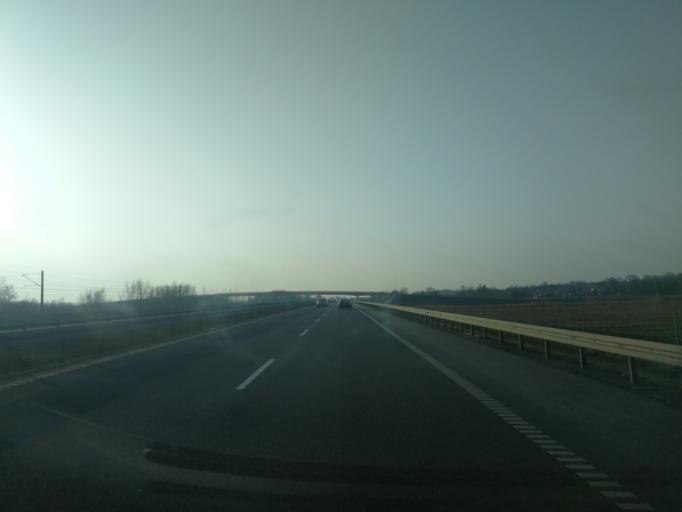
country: PL
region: Warmian-Masurian Voivodeship
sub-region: Powiat elblaski
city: Gronowo Gorne
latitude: 54.1036
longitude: 19.5209
